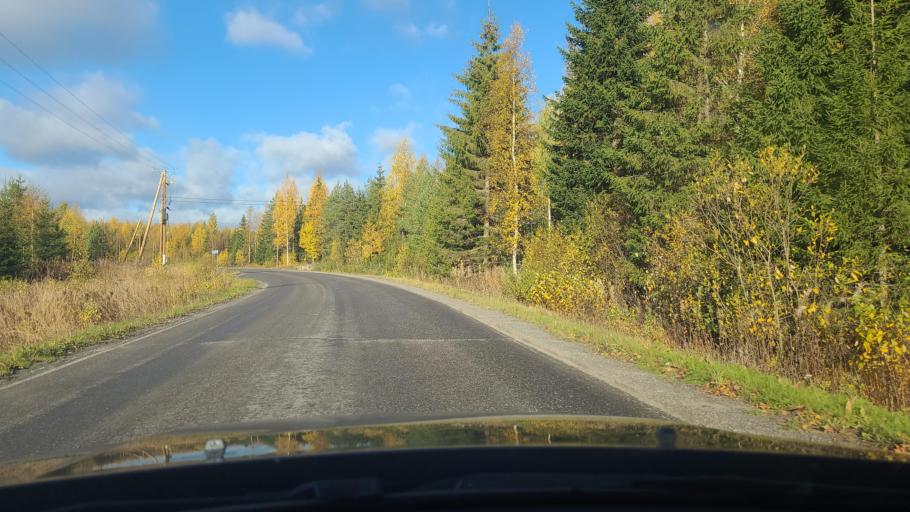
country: FI
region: Southern Savonia
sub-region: Pieksaemaeki
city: Juva
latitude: 61.8819
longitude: 27.7554
